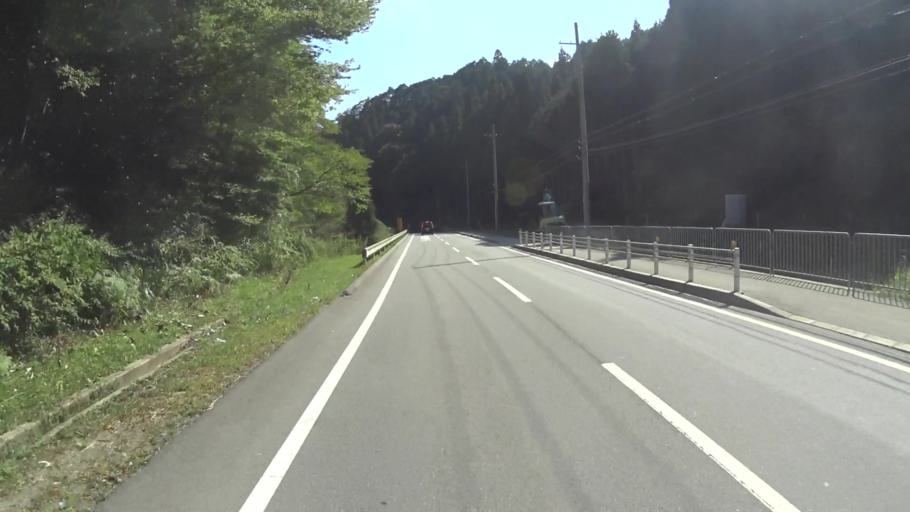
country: JP
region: Kyoto
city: Kameoka
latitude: 34.9602
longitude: 135.5561
